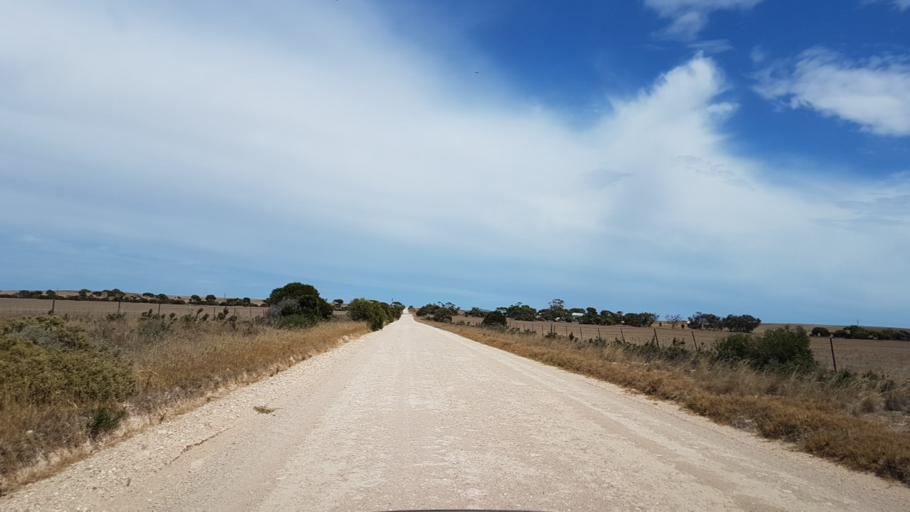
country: AU
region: South Australia
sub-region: Yorke Peninsula
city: Ardrossan
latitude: -34.3987
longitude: 137.9224
